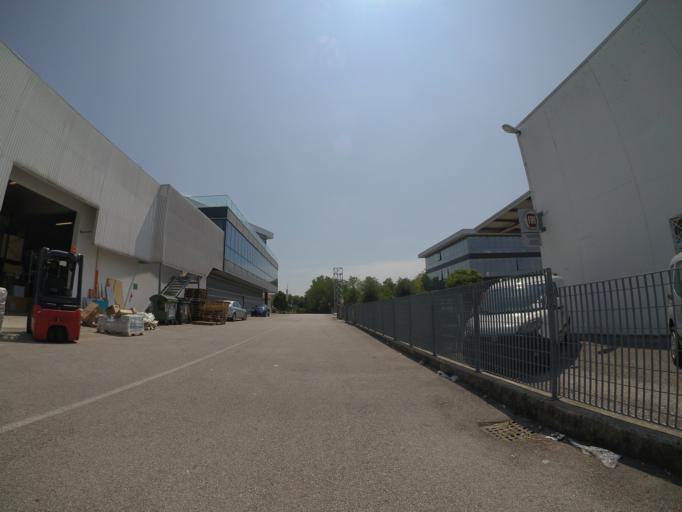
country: IT
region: Friuli Venezia Giulia
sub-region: Provincia di Udine
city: Codroipo
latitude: 45.9668
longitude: 12.9710
